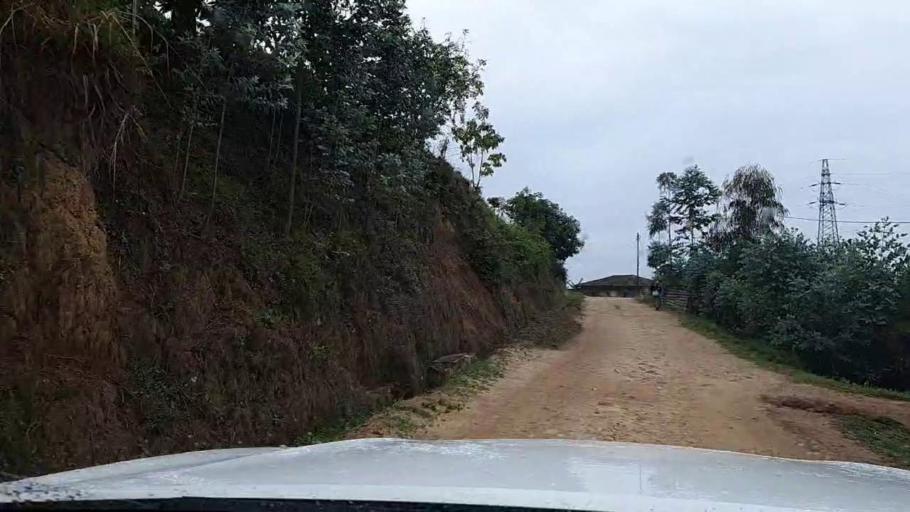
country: RW
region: Southern Province
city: Nzega
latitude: -2.4571
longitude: 29.4940
